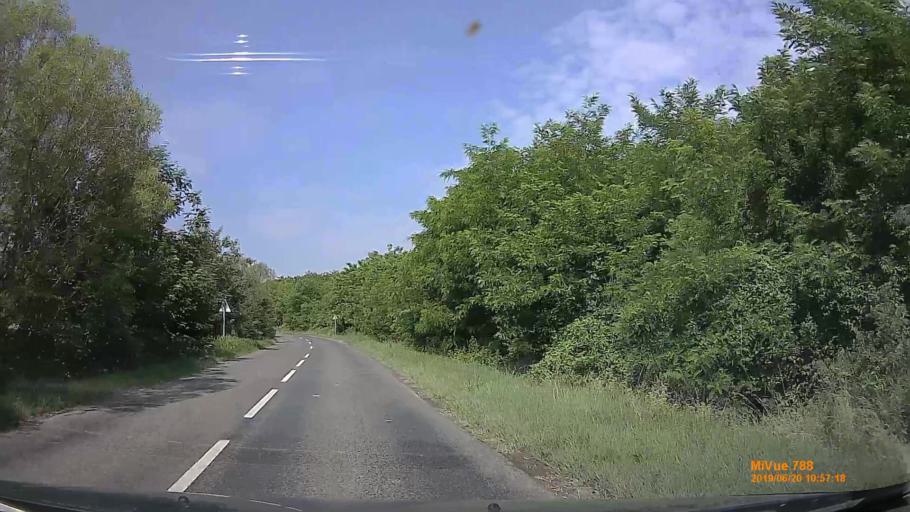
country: HU
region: Baranya
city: Mecseknadasd
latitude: 46.1535
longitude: 18.5229
